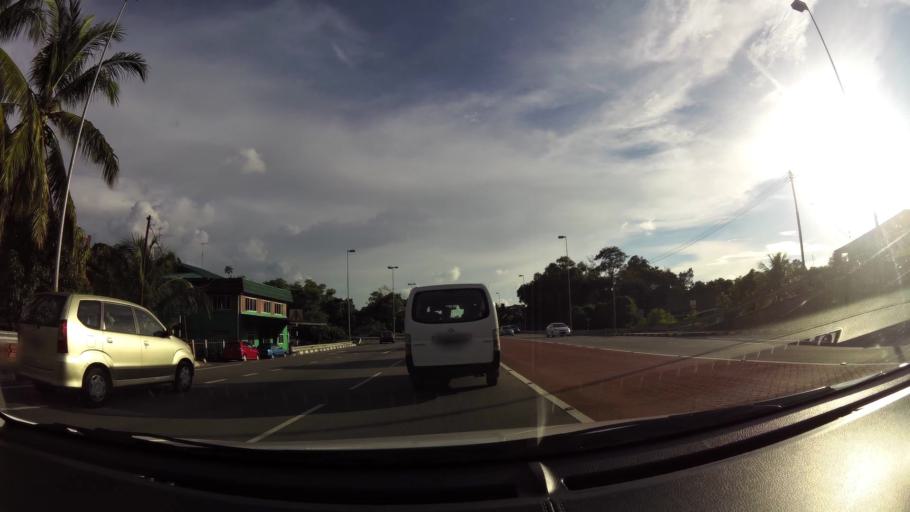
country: BN
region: Brunei and Muara
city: Bandar Seri Begawan
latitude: 4.9718
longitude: 114.9805
